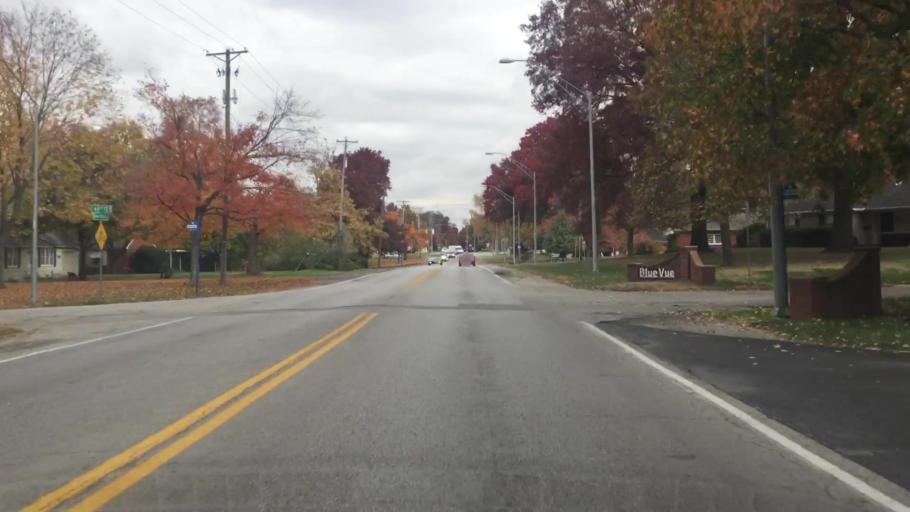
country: US
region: Missouri
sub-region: Jackson County
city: Raytown
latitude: 39.0336
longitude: -94.4390
